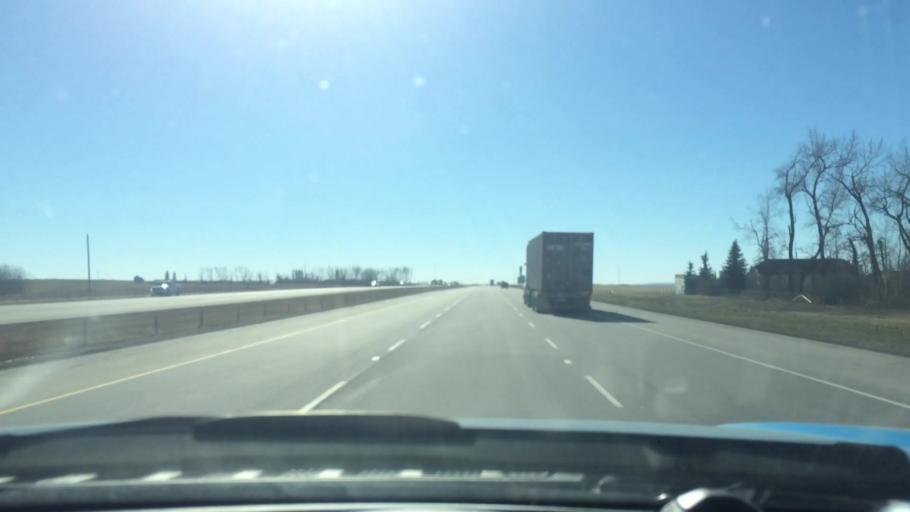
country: CA
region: Alberta
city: Crossfield
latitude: 51.4050
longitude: -114.0021
